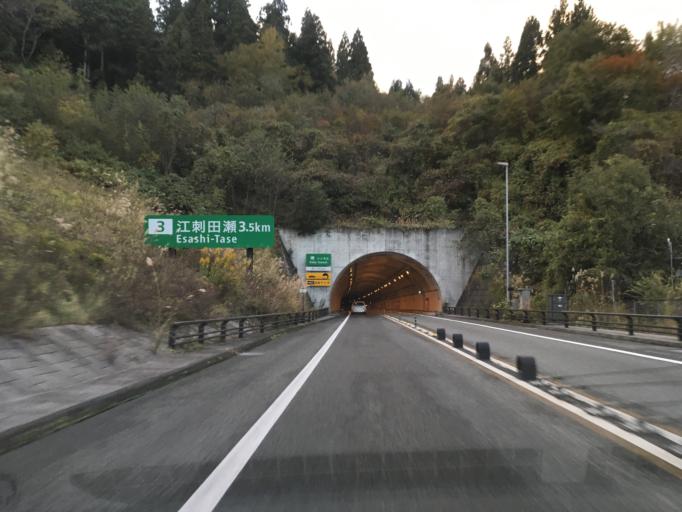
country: JP
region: Iwate
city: Kitakami
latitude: 39.2935
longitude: 141.3139
